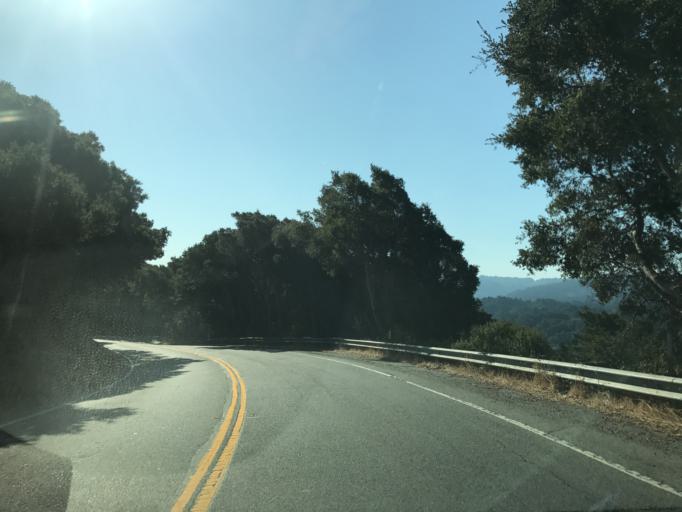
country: US
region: California
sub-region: San Mateo County
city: Highlands-Baywood Park
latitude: 37.5199
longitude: -122.3562
